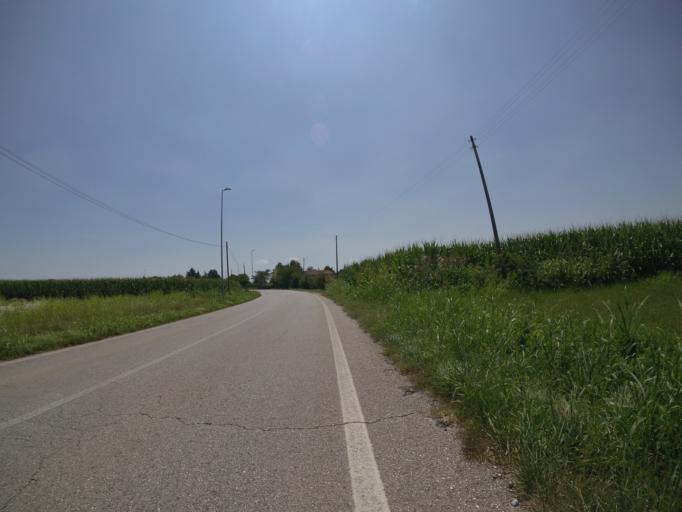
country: IT
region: Friuli Venezia Giulia
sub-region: Provincia di Udine
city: Lestizza
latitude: 45.9709
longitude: 13.1394
